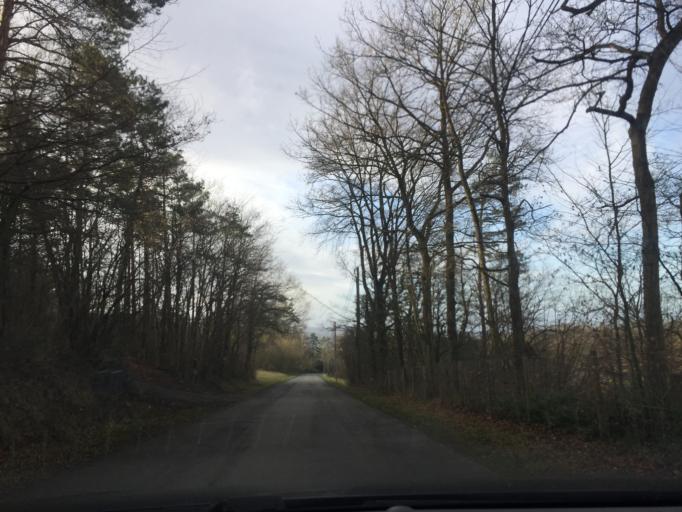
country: BE
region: Wallonia
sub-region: Province du Luxembourg
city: Hotton
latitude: 50.3009
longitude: 5.4954
